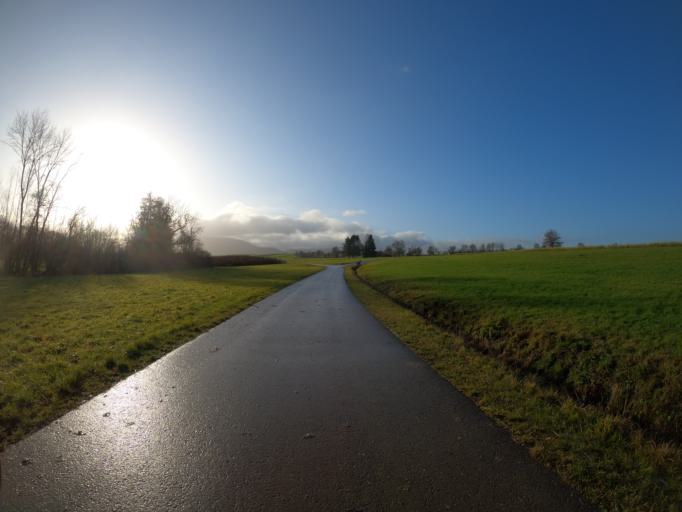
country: DE
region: Baden-Wuerttemberg
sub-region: Regierungsbezirk Stuttgart
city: Boll
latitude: 48.6611
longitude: 9.6237
